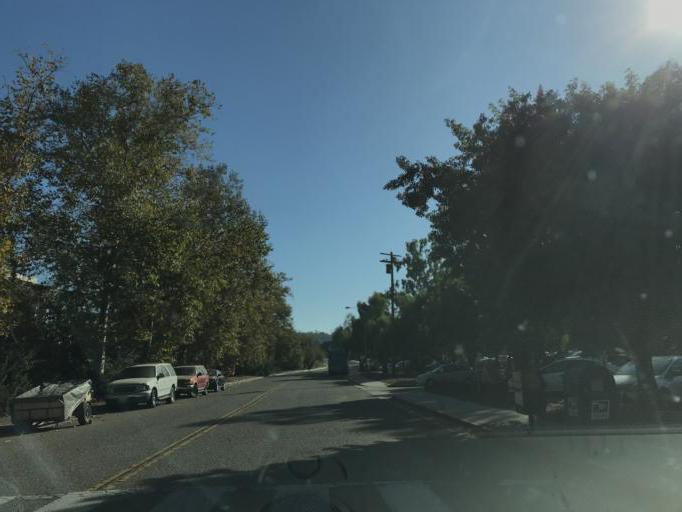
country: US
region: California
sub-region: Santa Barbara County
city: Goleta
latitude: 34.4449
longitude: -119.7794
